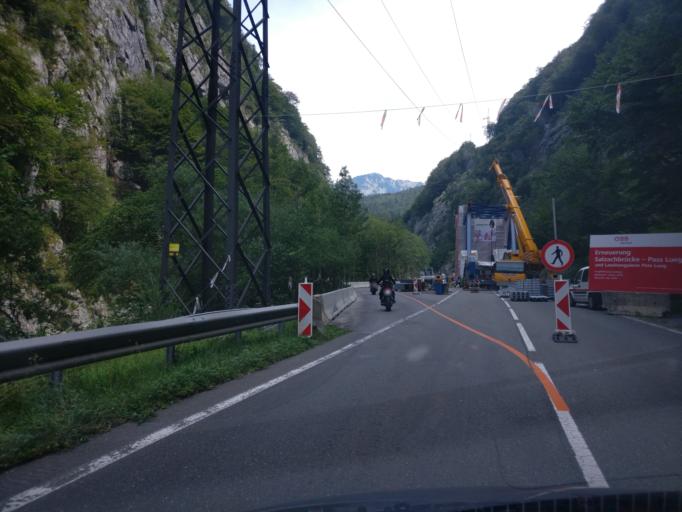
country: AT
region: Salzburg
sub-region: Politischer Bezirk Hallein
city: Golling an der Salzach
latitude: 47.5686
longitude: 13.1857
